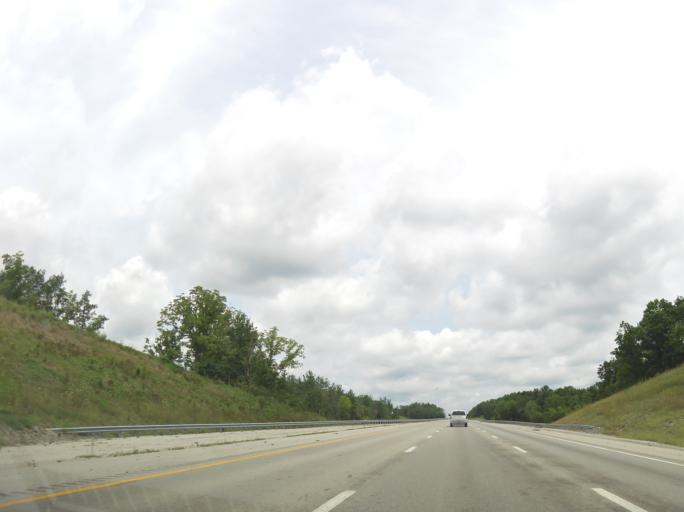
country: US
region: Kentucky
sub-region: Grant County
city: Williamstown
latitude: 38.4519
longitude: -84.5728
